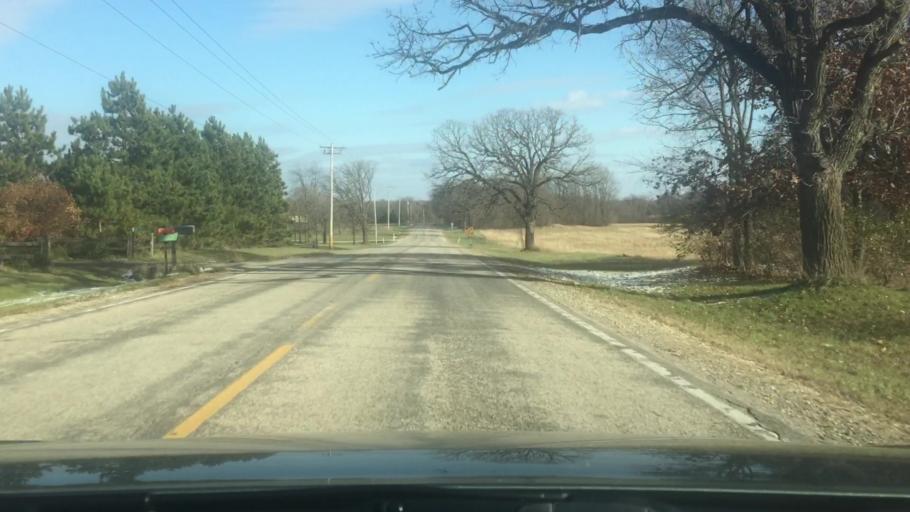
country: US
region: Wisconsin
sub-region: Jefferson County
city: Palmyra
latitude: 42.9397
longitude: -88.5989
